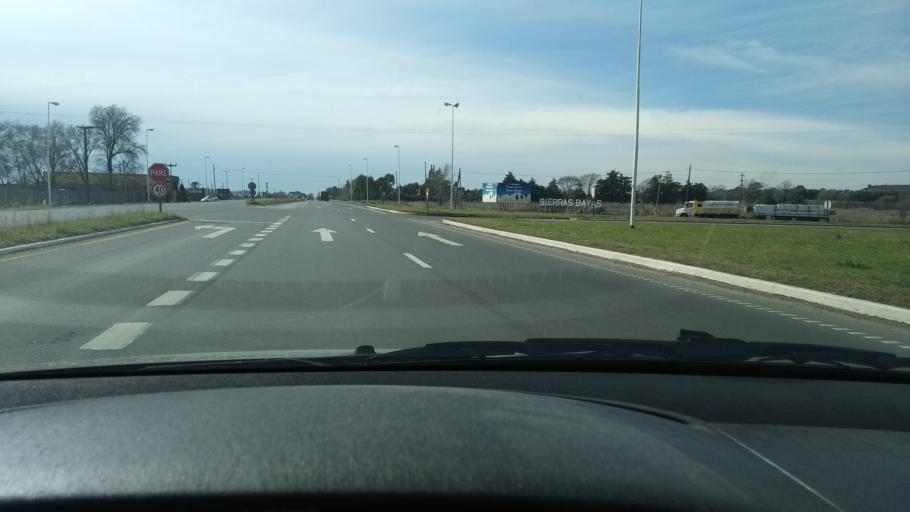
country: AR
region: Buenos Aires
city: Olavarria
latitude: -36.9169
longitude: -60.2050
